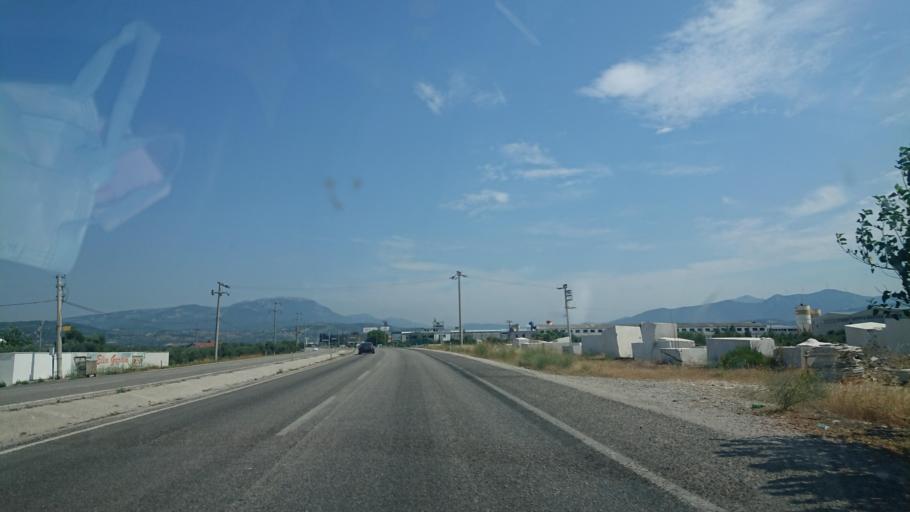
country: TR
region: Izmir
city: Torbali
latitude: 38.2189
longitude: 27.3701
